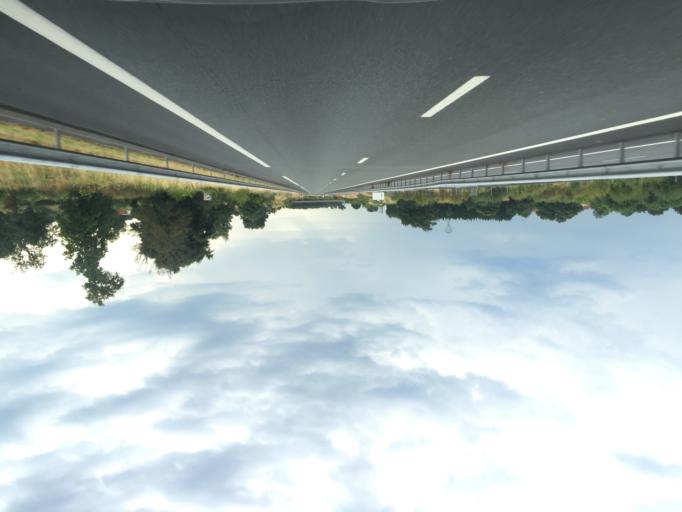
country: FR
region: Rhone-Alpes
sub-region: Departement de la Loire
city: La Pacaudiere
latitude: 46.1508
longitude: 3.8960
